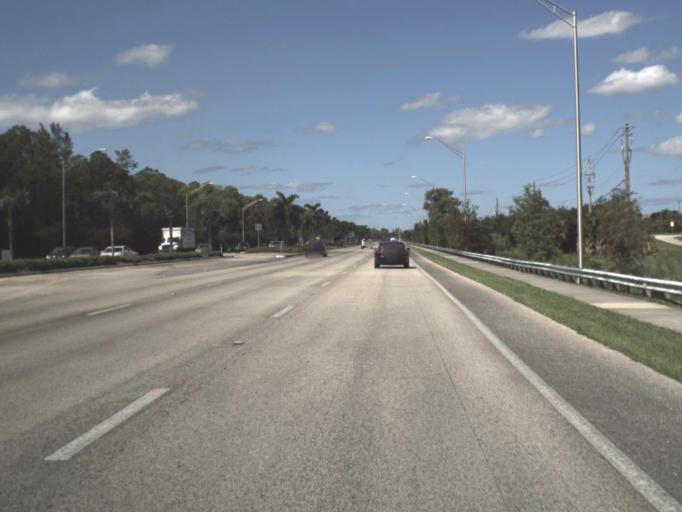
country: US
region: Florida
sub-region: Collier County
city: Lely Resort
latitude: 26.0710
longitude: -81.7110
